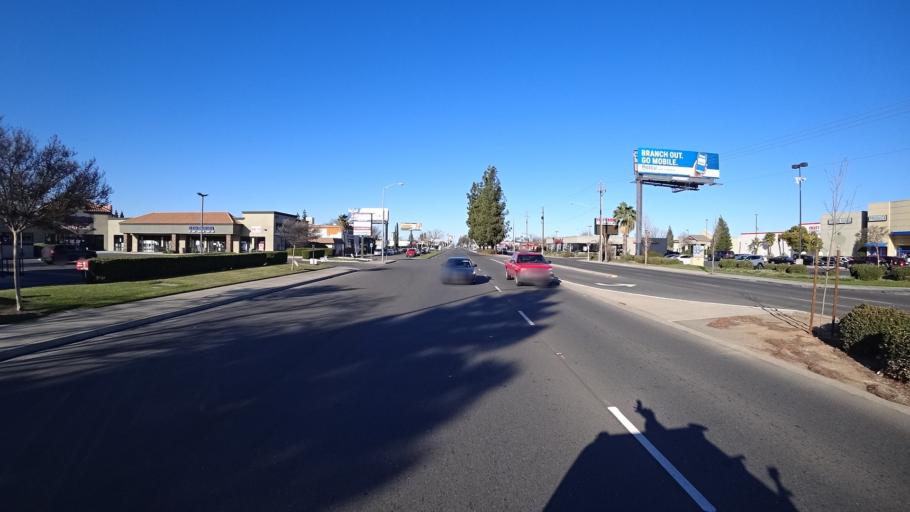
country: US
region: California
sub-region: Fresno County
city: West Park
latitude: 36.8082
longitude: -119.8663
